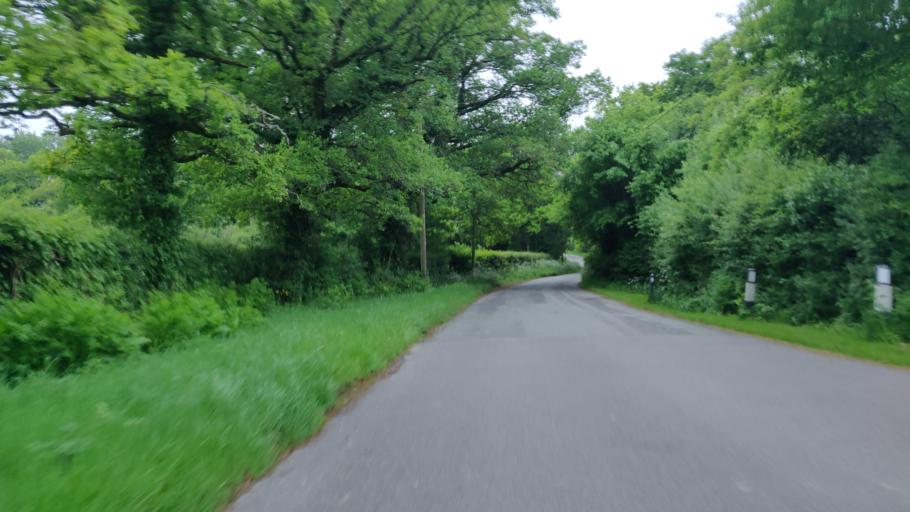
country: GB
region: England
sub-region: West Sussex
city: Southwater
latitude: 51.0111
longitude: -0.3265
